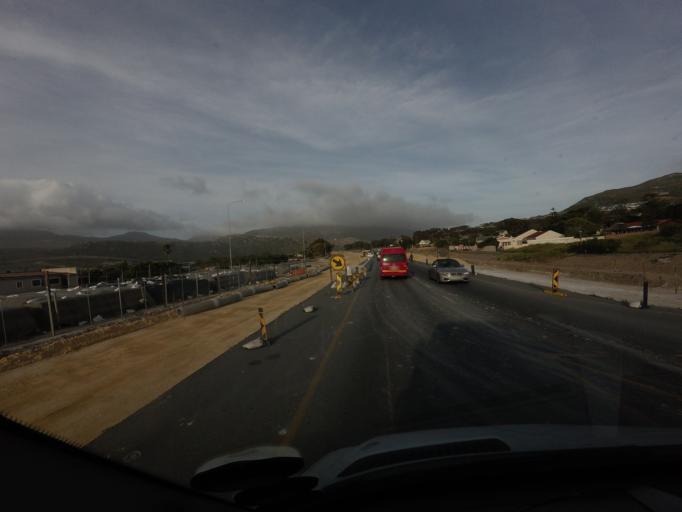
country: ZA
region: Western Cape
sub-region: City of Cape Town
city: Bergvliet
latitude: -34.1290
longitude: 18.3933
